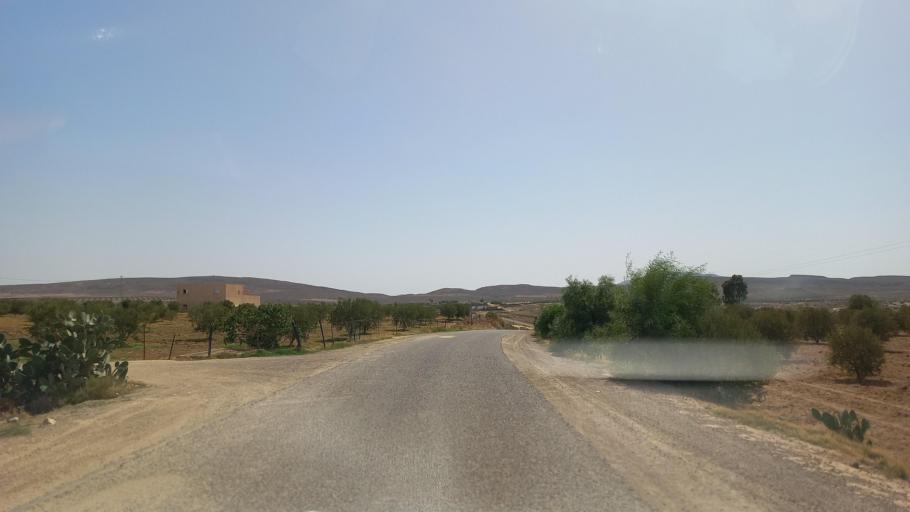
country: TN
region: Al Qasrayn
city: Kasserine
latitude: 35.2102
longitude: 9.0413
